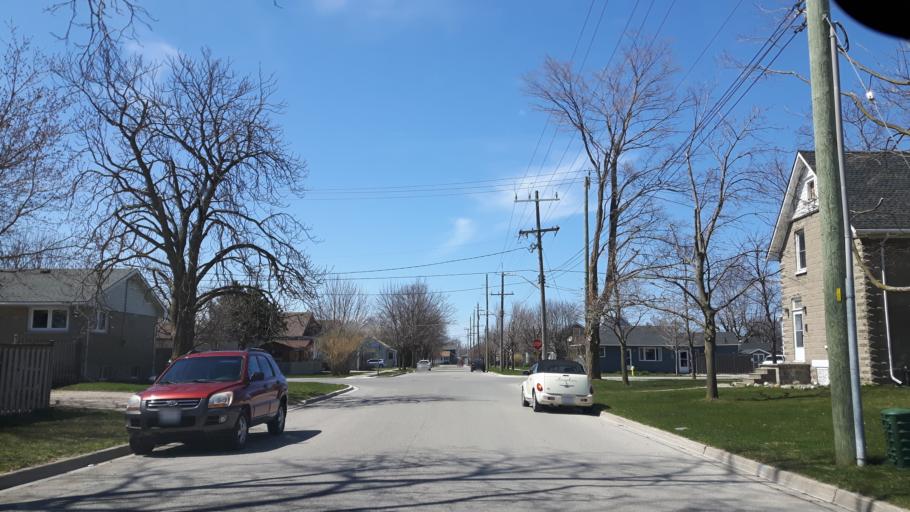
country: CA
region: Ontario
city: Goderich
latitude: 43.7382
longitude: -81.6994
